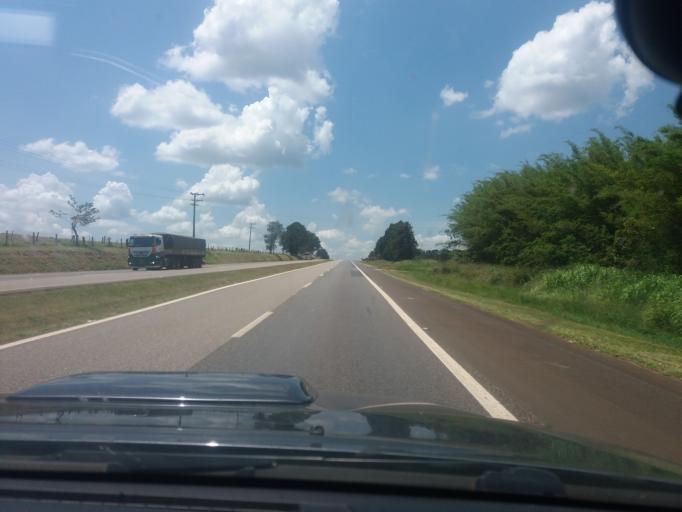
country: BR
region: Sao Paulo
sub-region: Itapetininga
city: Itapetininga
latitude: -23.5154
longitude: -47.9674
